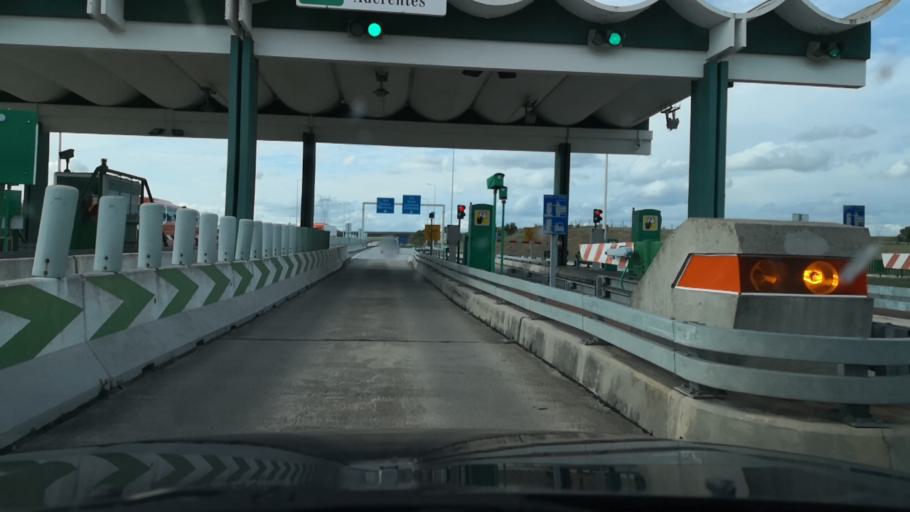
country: PT
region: Evora
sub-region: Evora
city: Evora
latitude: 38.6433
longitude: -7.8551
